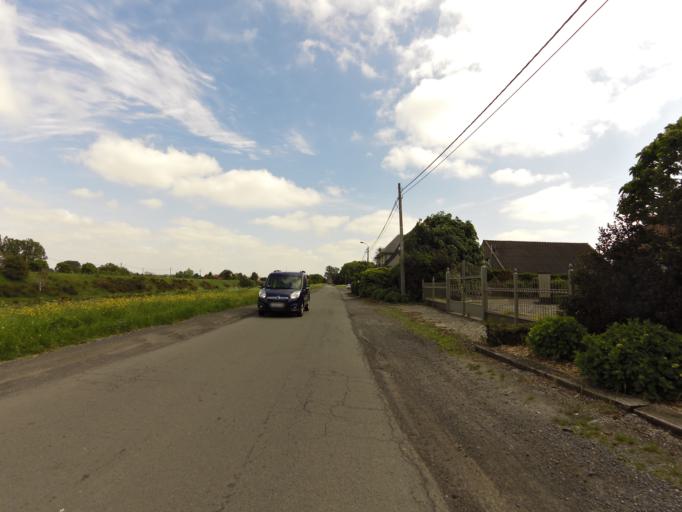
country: BE
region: Flanders
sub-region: Provincie Oost-Vlaanderen
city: Knesselare
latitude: 51.1157
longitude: 3.3937
